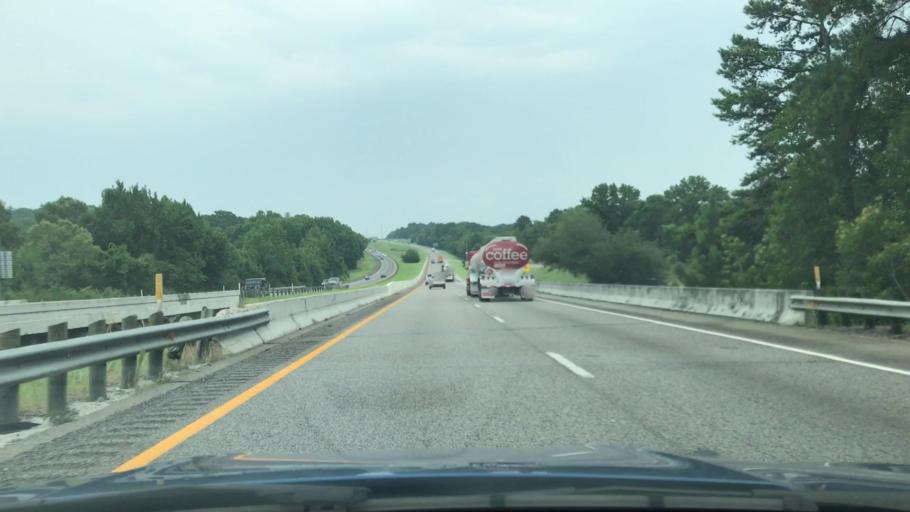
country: US
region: Texas
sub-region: Smith County
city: Tyler
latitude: 32.4583
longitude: -95.3112
